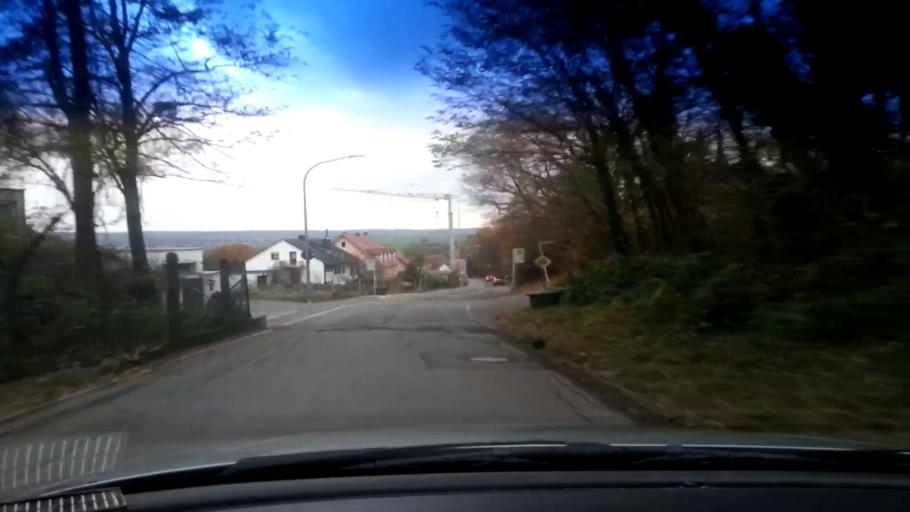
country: DE
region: Bavaria
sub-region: Upper Franconia
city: Stegaurach
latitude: 49.8830
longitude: 10.8620
